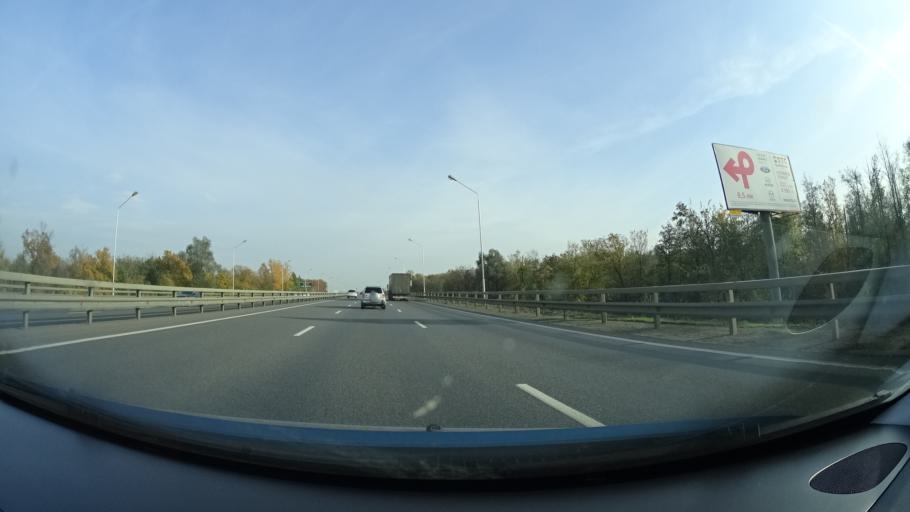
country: RU
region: Bashkortostan
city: Ufa
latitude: 54.6524
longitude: 55.9028
